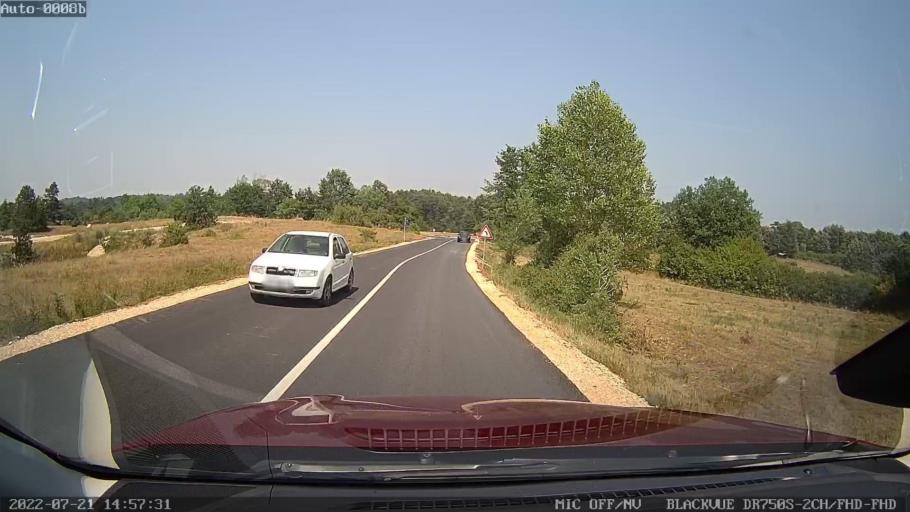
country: HR
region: Istarska
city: Pazin
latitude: 45.2095
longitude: 13.9530
